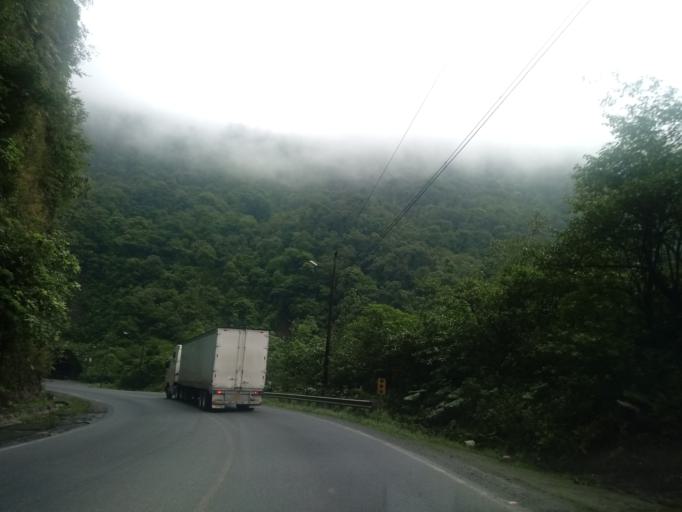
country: CR
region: Heredia
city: Angeles
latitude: 10.0591
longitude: -84.0081
